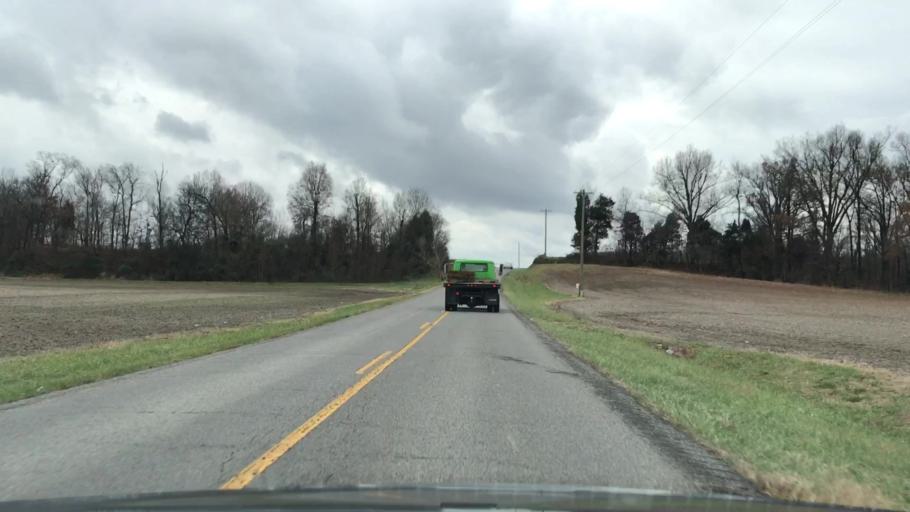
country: US
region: Kentucky
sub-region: Webster County
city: Sebree
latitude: 37.5012
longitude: -87.4350
